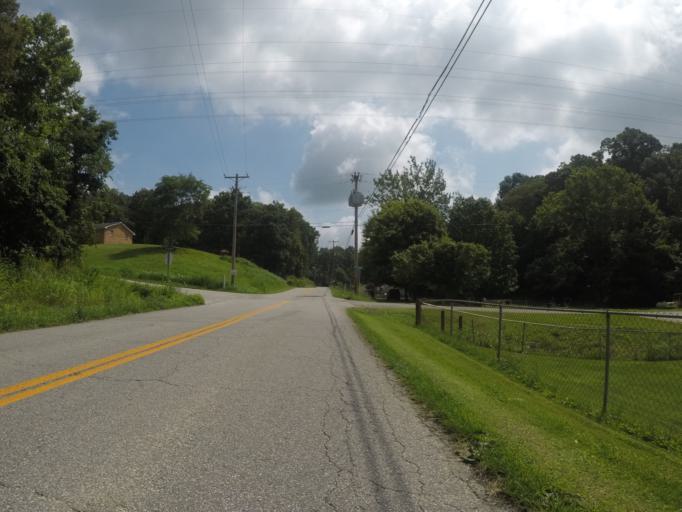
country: US
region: Kentucky
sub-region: Boyd County
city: Catlettsburg
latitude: 38.4019
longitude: -82.6496
